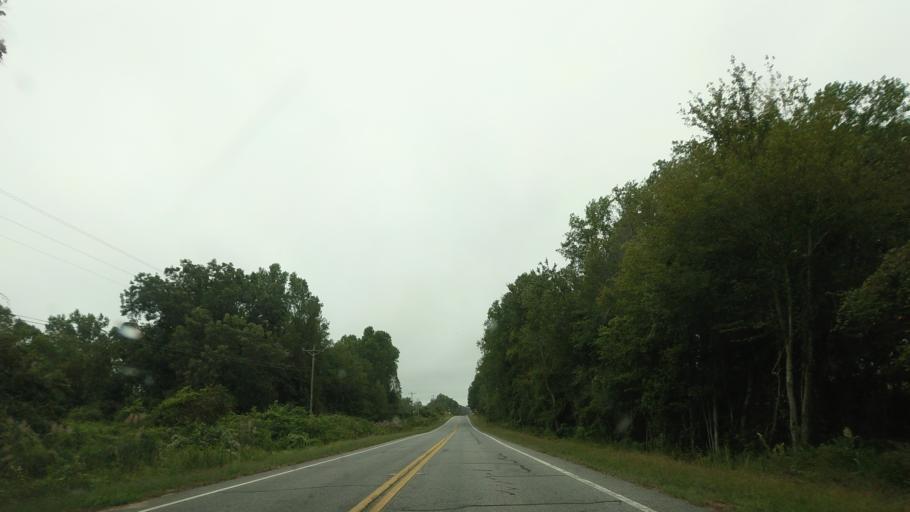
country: US
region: Georgia
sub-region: Irwin County
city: Ocilla
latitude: 31.4827
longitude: -83.2380
